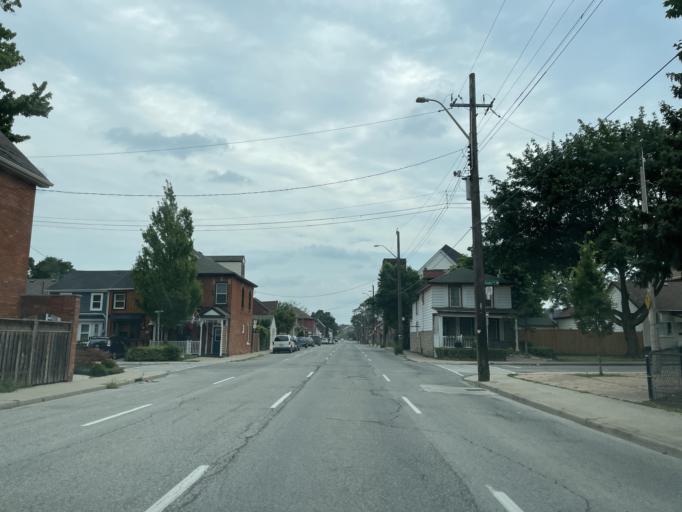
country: CA
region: Ontario
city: Hamilton
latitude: 43.2555
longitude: -79.8547
